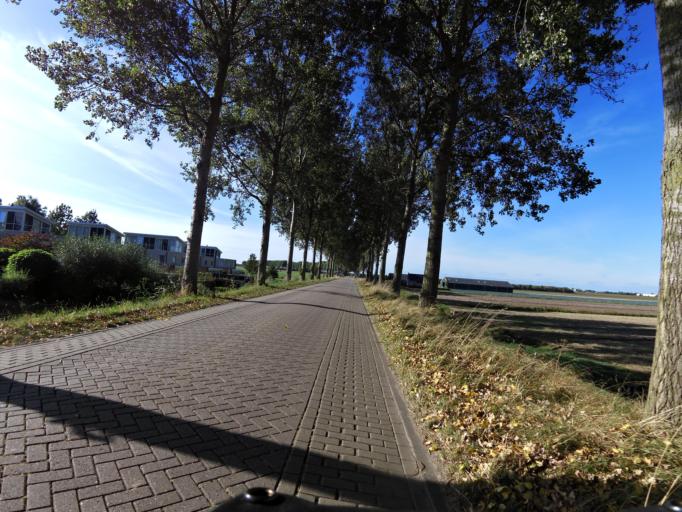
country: NL
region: South Holland
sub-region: Gemeente Zwijndrecht
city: Zwijndrecht
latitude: 51.7877
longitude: 4.6068
